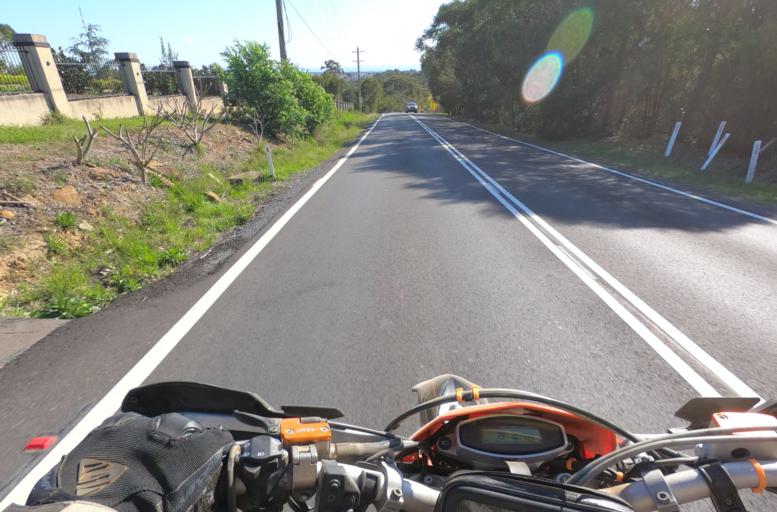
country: AU
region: New South Wales
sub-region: The Hills Shire
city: Glenhaven
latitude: -33.6881
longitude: 150.9819
